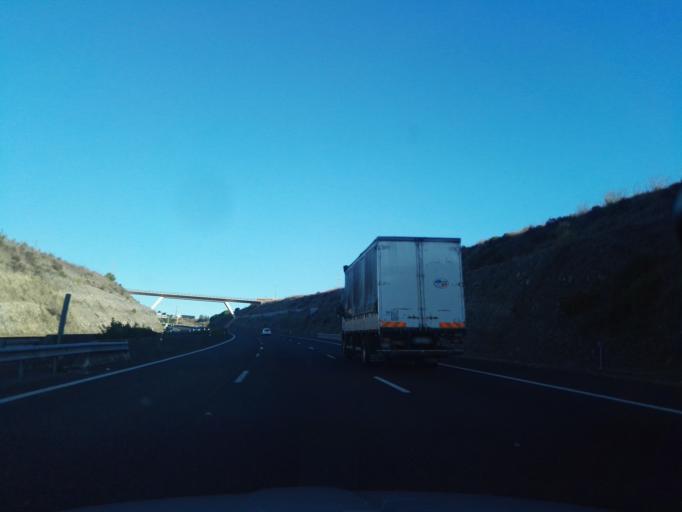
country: PT
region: Lisbon
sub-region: Vila Franca de Xira
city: Vialonga
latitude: 38.9155
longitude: -9.0726
